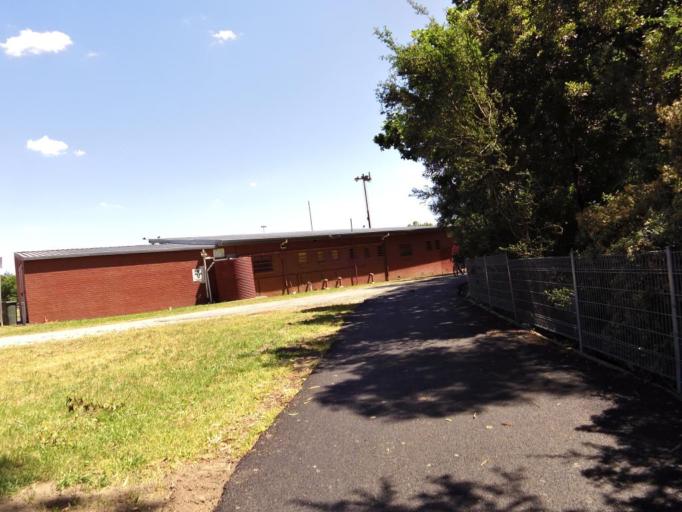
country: AU
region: Victoria
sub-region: Knox
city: Ferntree Gully
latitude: -37.8898
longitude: 145.2942
